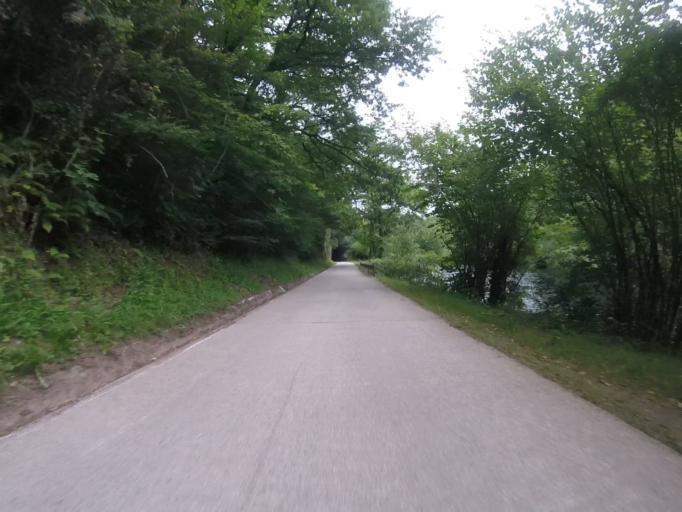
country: ES
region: Navarre
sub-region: Provincia de Navarra
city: Doneztebe
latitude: 43.1417
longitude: -1.6669
